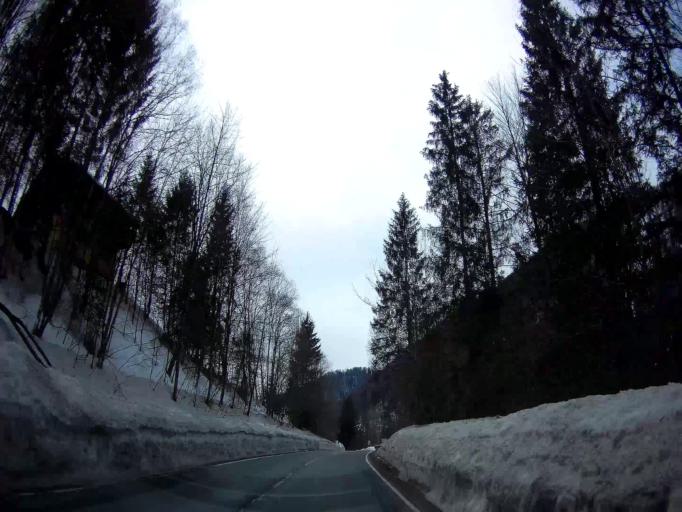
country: AT
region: Salzburg
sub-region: Politischer Bezirk Hallein
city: Krispl
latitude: 47.7387
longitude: 13.1625
